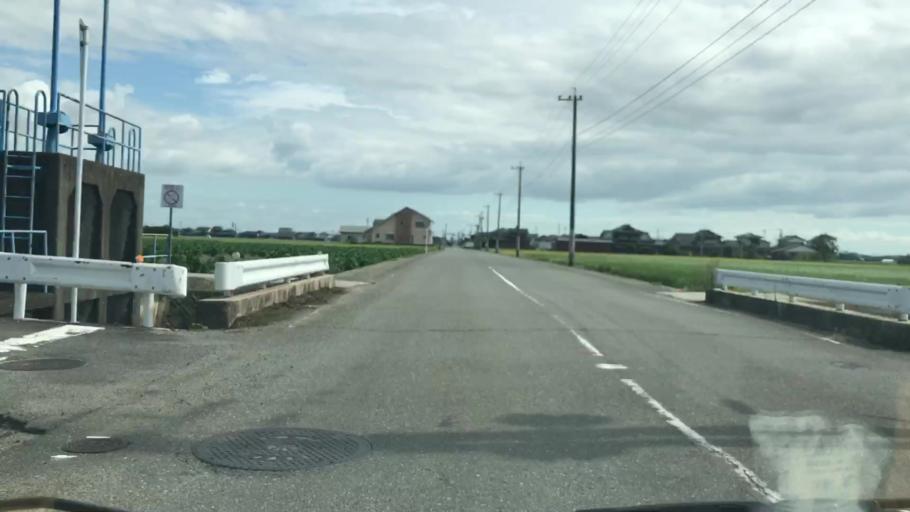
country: JP
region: Saga Prefecture
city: Saga-shi
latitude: 33.2233
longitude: 130.1767
